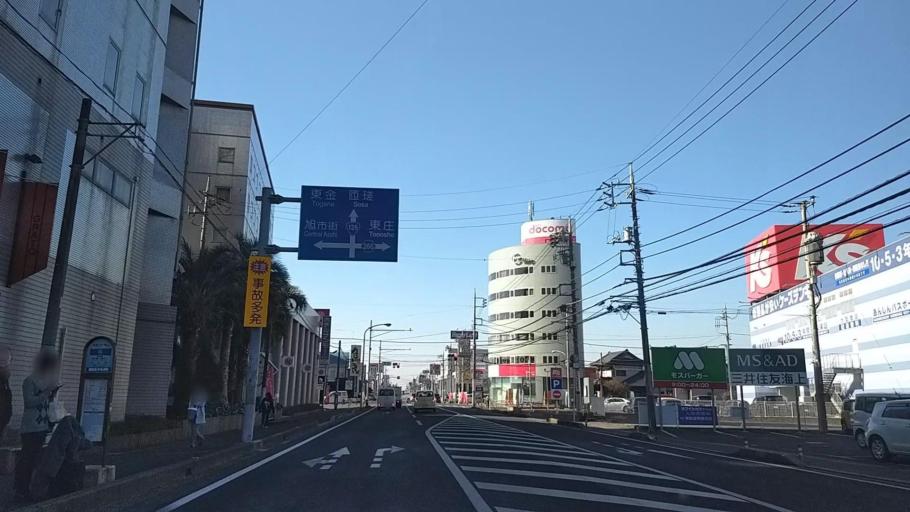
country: JP
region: Chiba
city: Asahi
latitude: 35.7258
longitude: 140.6595
